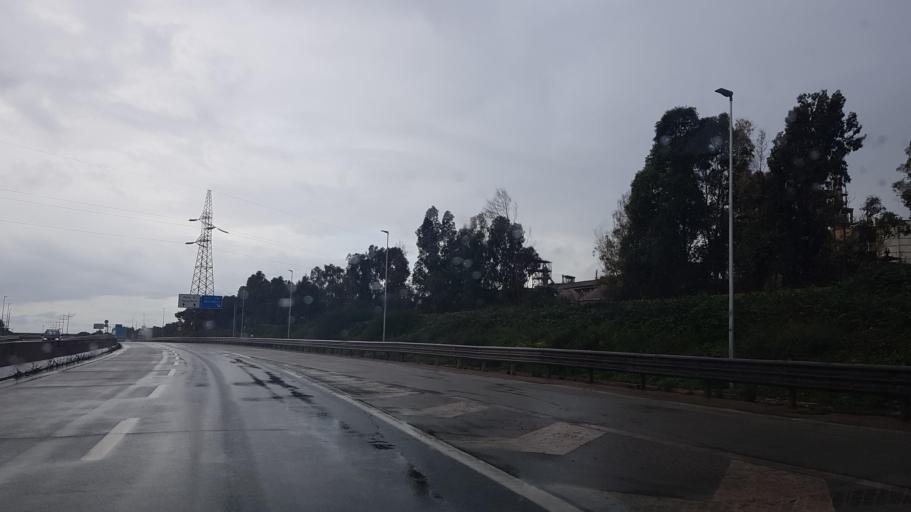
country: IT
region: Apulia
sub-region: Provincia di Taranto
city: Statte
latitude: 40.4888
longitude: 17.2088
